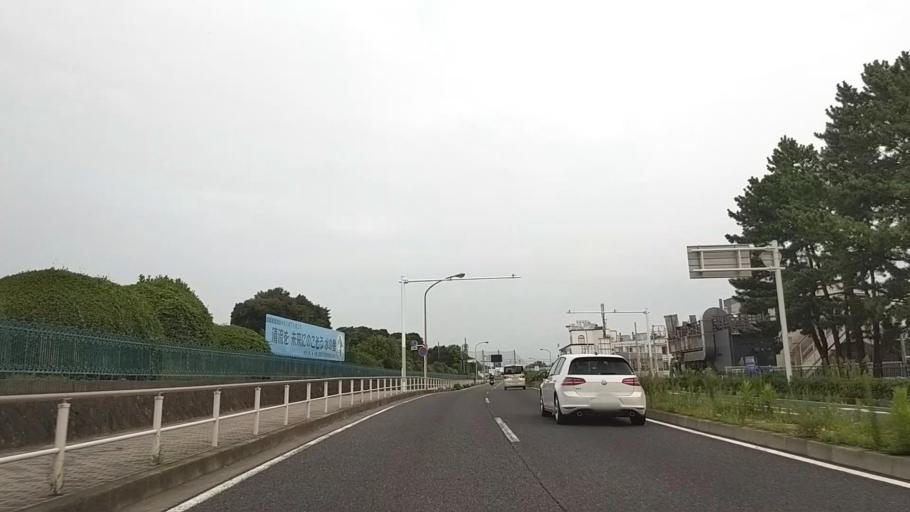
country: JP
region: Kanagawa
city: Chigasaki
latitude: 35.3178
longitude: 139.3811
